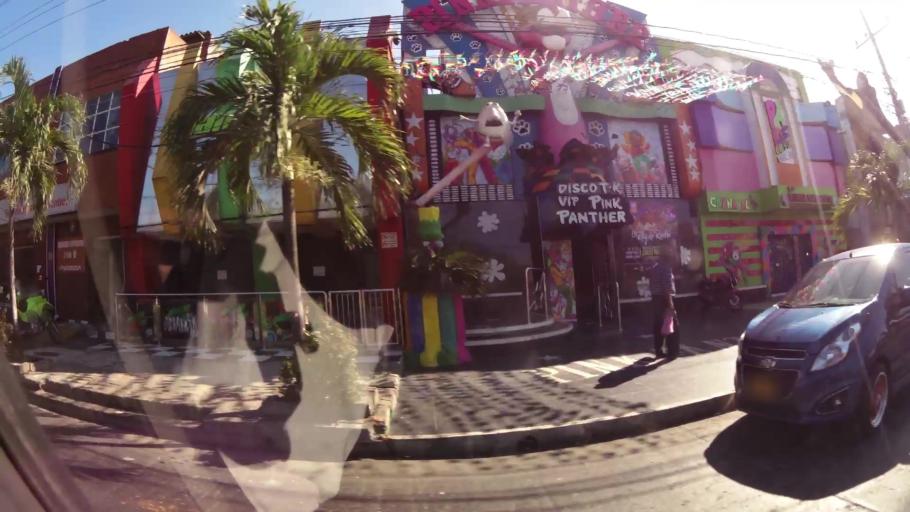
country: CO
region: Atlantico
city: Barranquilla
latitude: 10.9461
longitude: -74.7976
